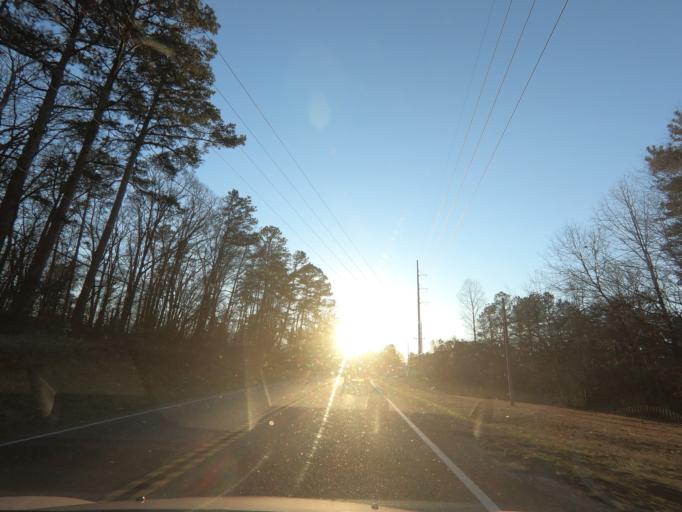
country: US
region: Georgia
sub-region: Forsyth County
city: Cumming
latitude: 34.2999
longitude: -84.1696
